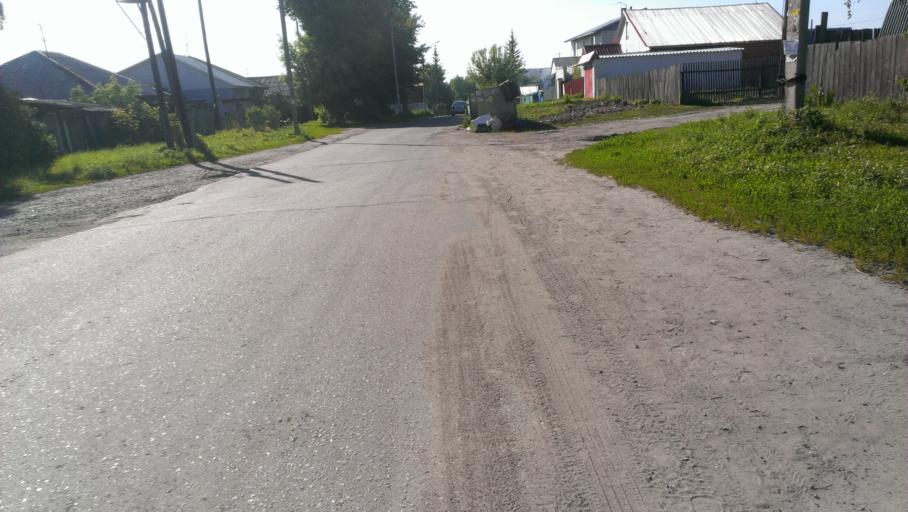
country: RU
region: Altai Krai
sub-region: Gorod Barnaulskiy
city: Barnaul
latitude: 53.3551
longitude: 83.7514
